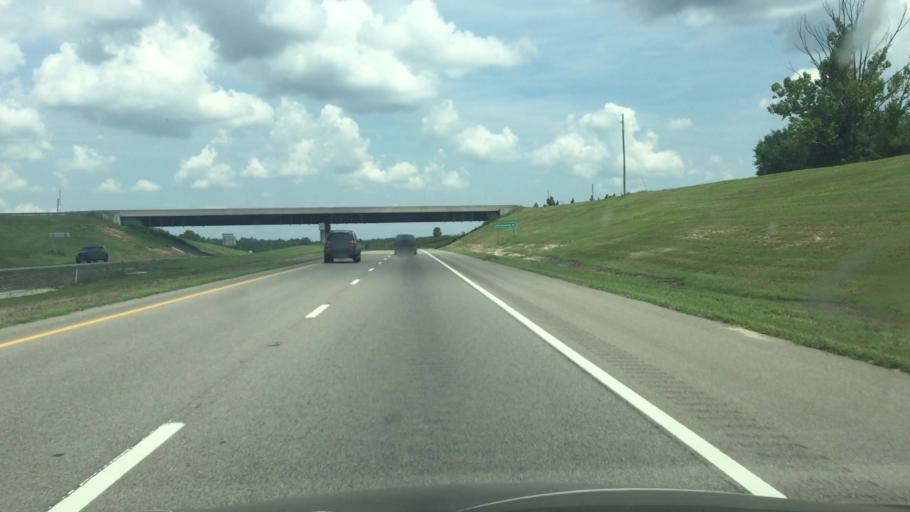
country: US
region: North Carolina
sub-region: Richmond County
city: Ellerbe
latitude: 35.1720
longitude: -79.7140
